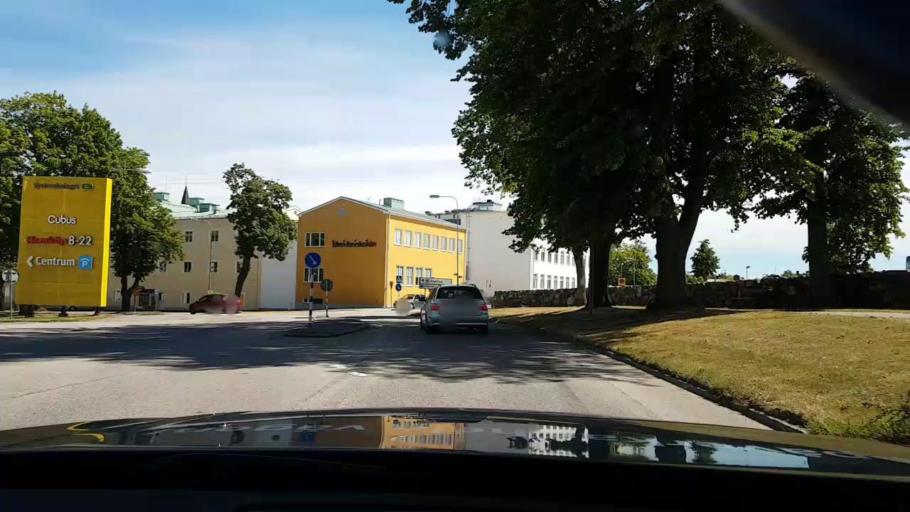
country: SE
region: Kalmar
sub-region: Vasterviks Kommun
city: Vaestervik
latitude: 57.7570
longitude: 16.6327
